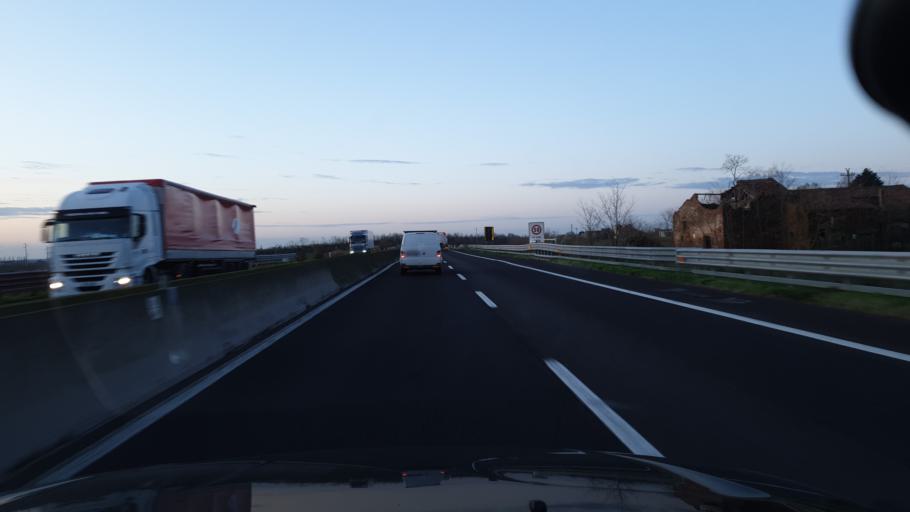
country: IT
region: Veneto
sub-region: Provincia di Rovigo
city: Villamarzana
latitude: 45.0006
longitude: 11.6750
